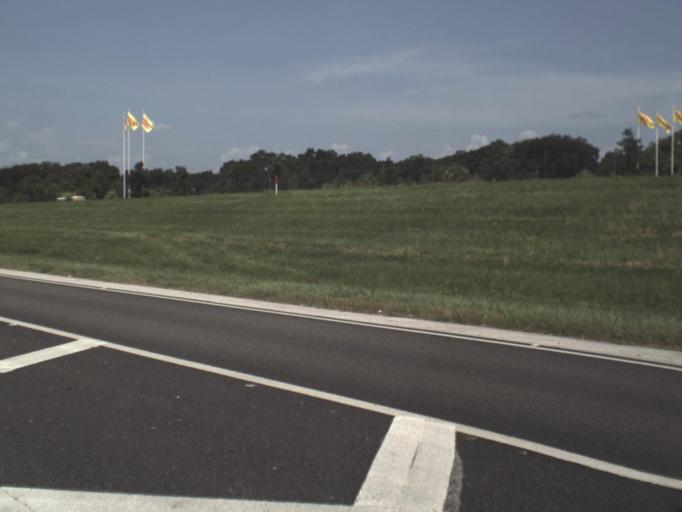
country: US
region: Florida
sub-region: Hillsborough County
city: Dover
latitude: 28.0272
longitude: -82.1923
